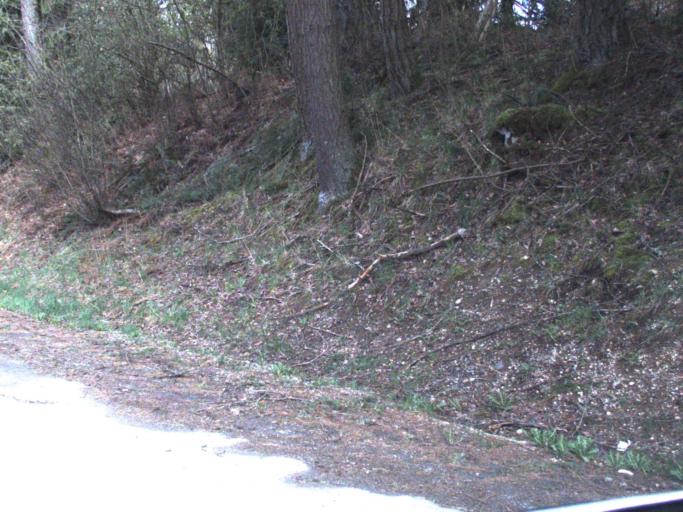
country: US
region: Washington
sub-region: King County
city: Black Diamond
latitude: 47.2966
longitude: -121.9996
